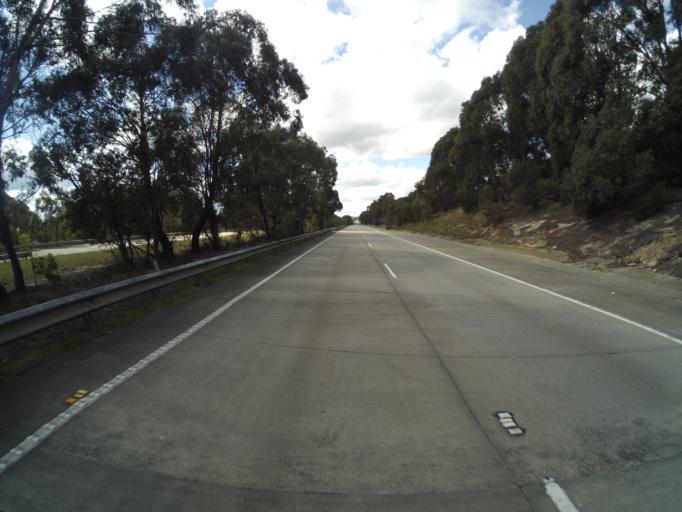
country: AU
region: New South Wales
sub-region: Wingecarribee
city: Bowral
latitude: -34.4461
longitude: 150.3877
